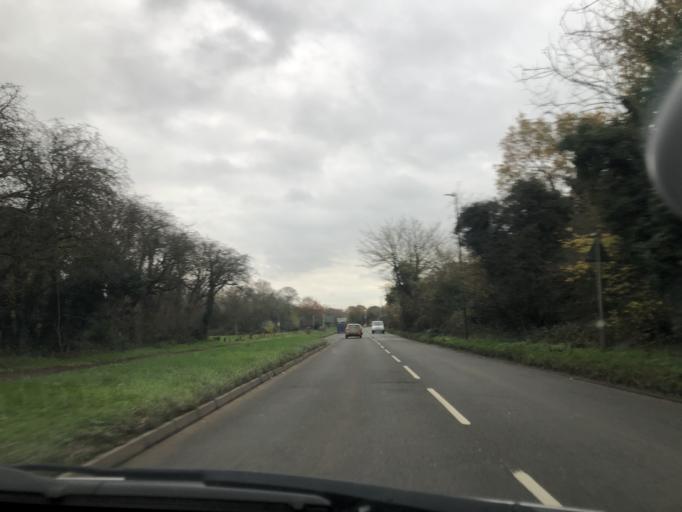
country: GB
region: England
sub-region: Greater London
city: Bexley
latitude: 51.4396
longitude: 0.1825
